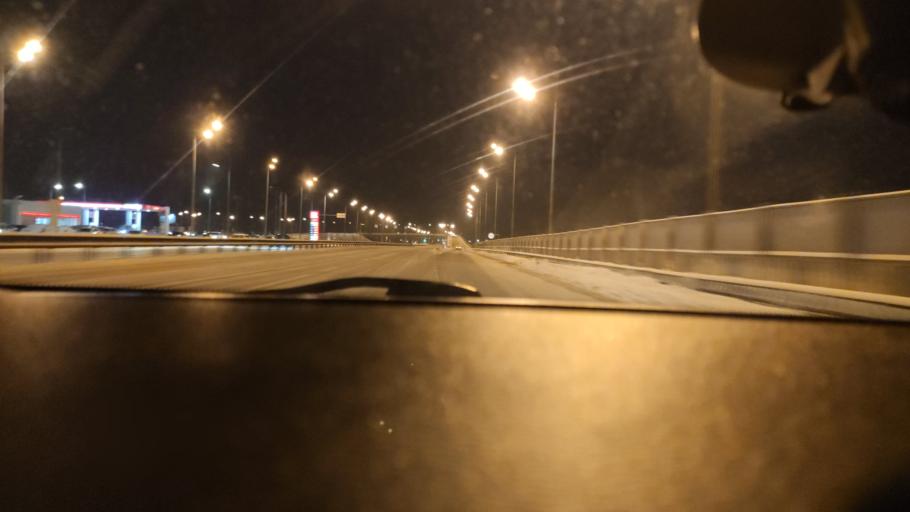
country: RU
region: Perm
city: Kultayevo
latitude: 57.9212
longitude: 56.0076
